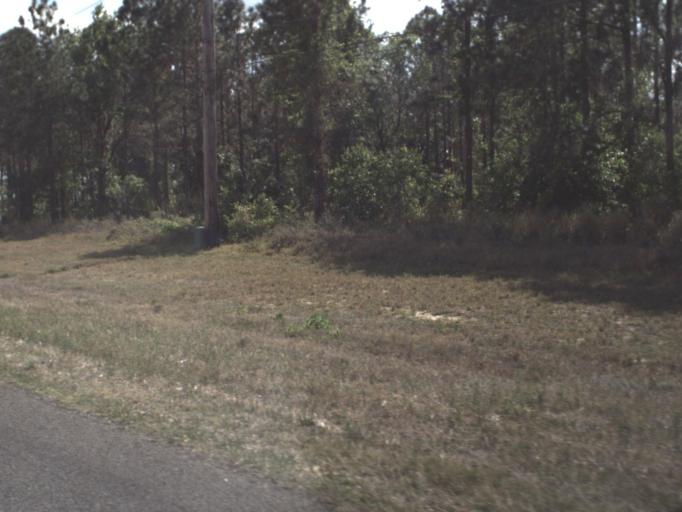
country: US
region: Florida
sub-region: Lake County
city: Minneola
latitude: 28.5930
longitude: -81.7528
